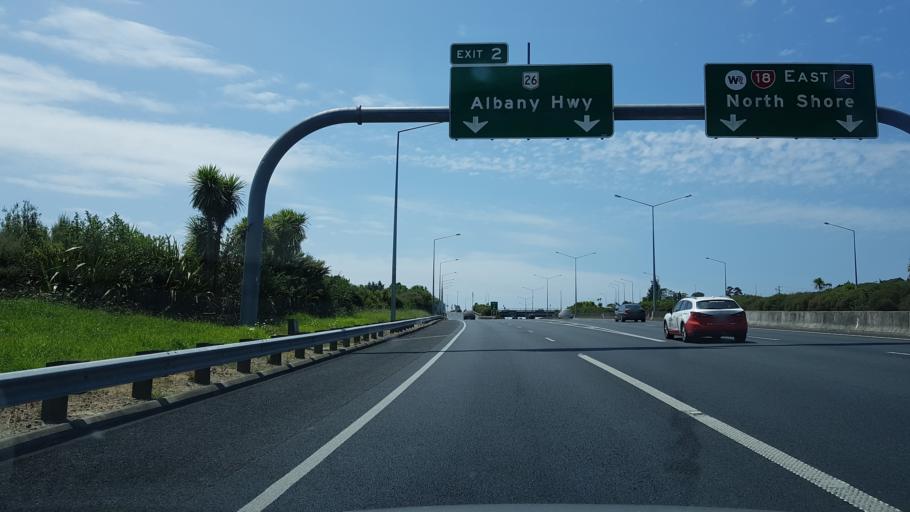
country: NZ
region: Auckland
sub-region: Auckland
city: Rothesay Bay
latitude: -36.7608
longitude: 174.7006
